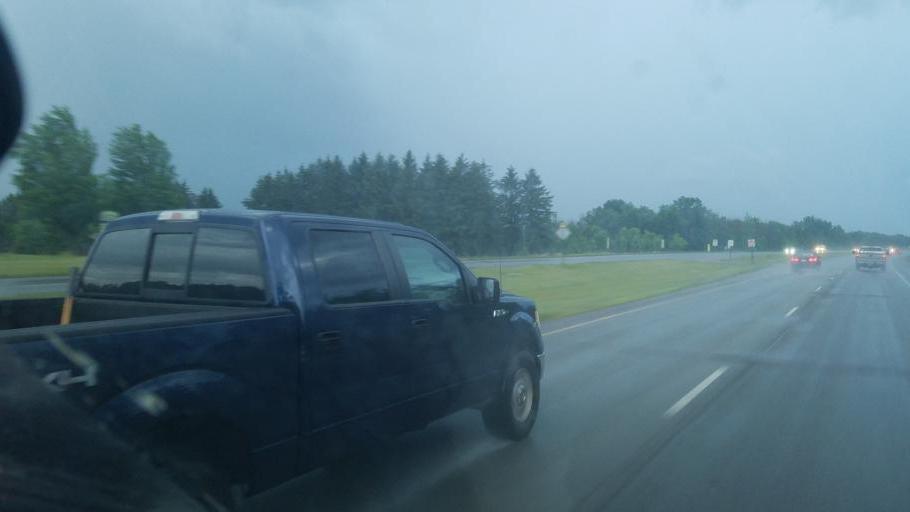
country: US
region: Ohio
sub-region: Summit County
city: Norton
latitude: 41.0016
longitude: -81.6619
